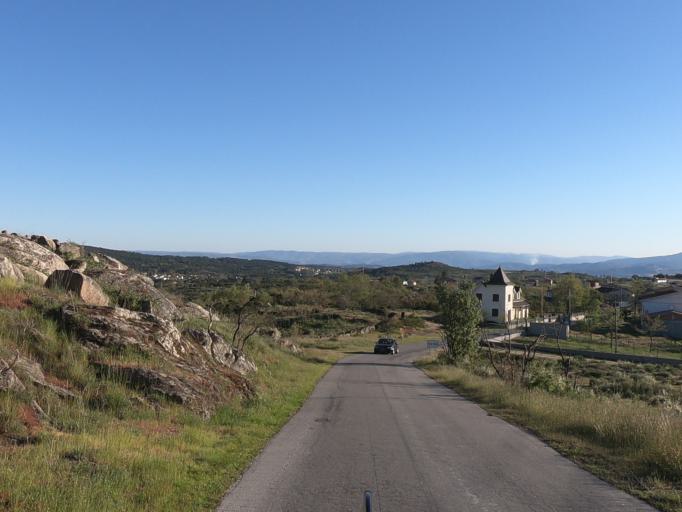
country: PT
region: Vila Real
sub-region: Vila Real
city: Vila Real
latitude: 41.3579
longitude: -7.6599
